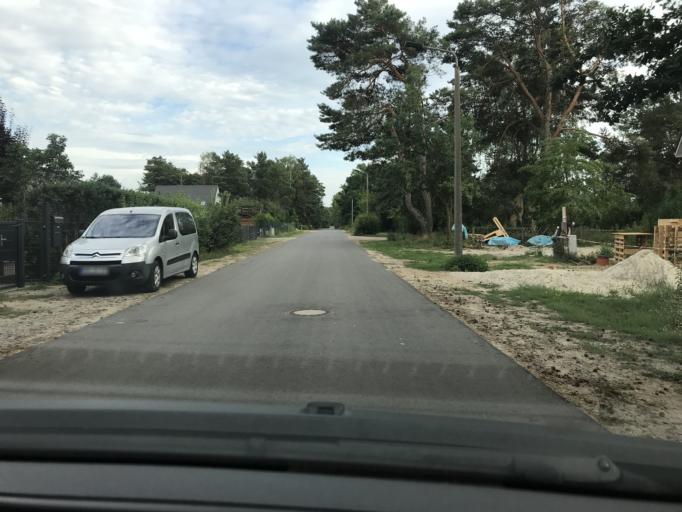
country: DE
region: Brandenburg
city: Wandlitz
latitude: 52.7109
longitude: 13.4465
